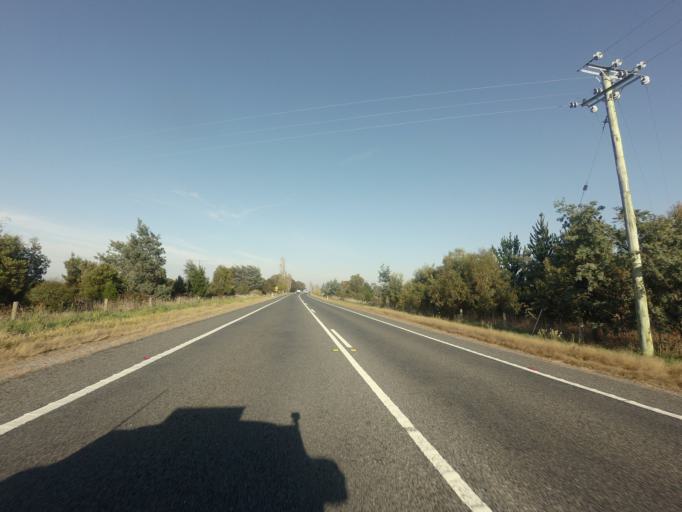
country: AU
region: Tasmania
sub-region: Northern Midlands
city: Longford
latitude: -41.5798
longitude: 147.1363
